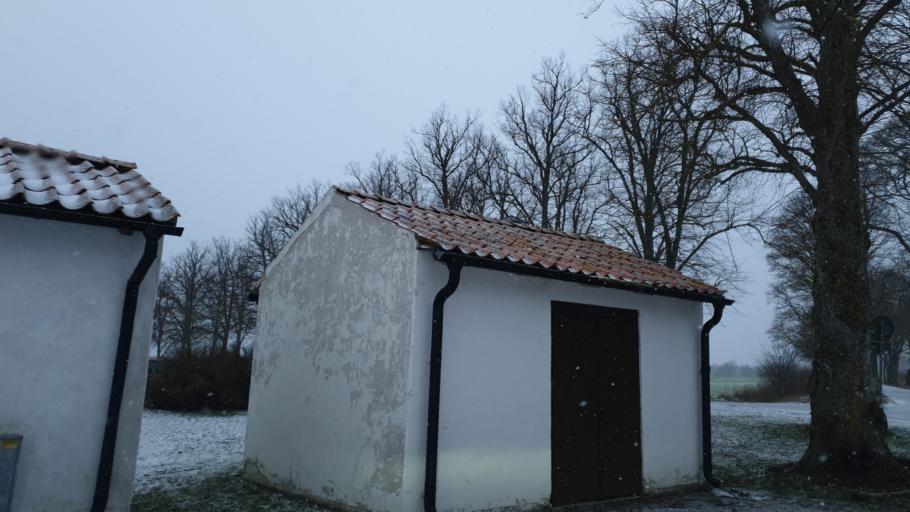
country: SE
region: Gotland
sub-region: Gotland
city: Visby
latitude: 57.5162
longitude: 18.4587
